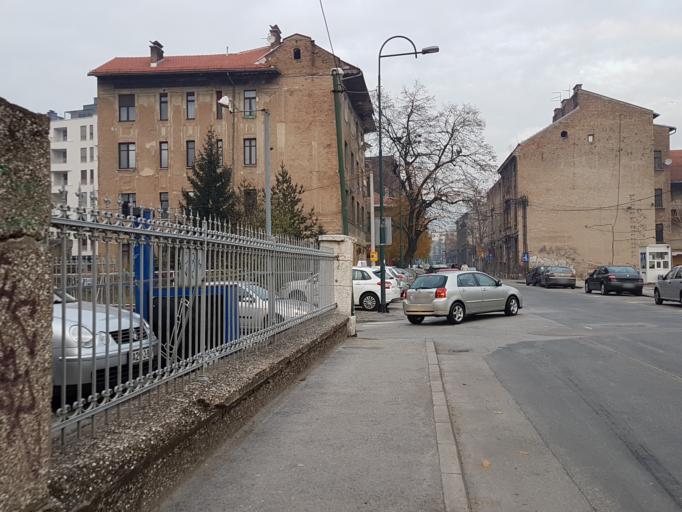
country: BA
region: Federation of Bosnia and Herzegovina
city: Kobilja Glava
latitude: 43.8548
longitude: 18.4092
